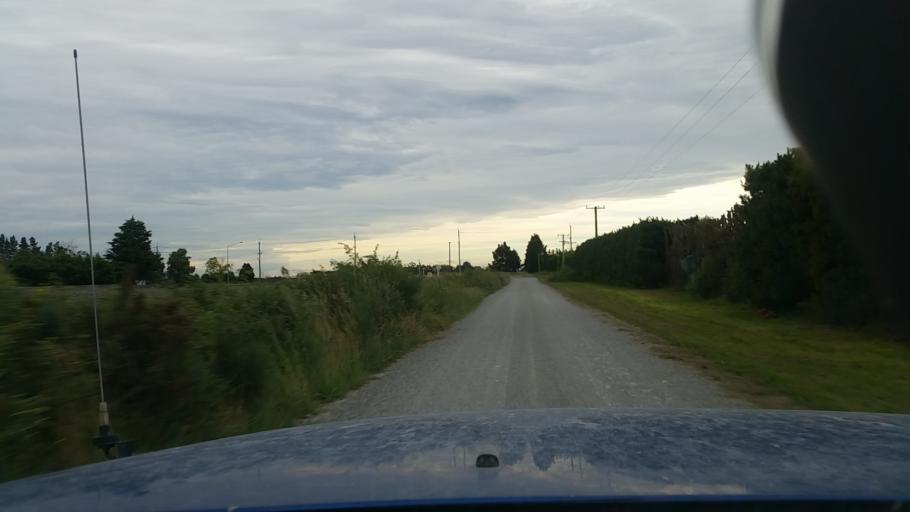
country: NZ
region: Canterbury
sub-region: Ashburton District
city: Tinwald
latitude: -43.9520
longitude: 171.6602
